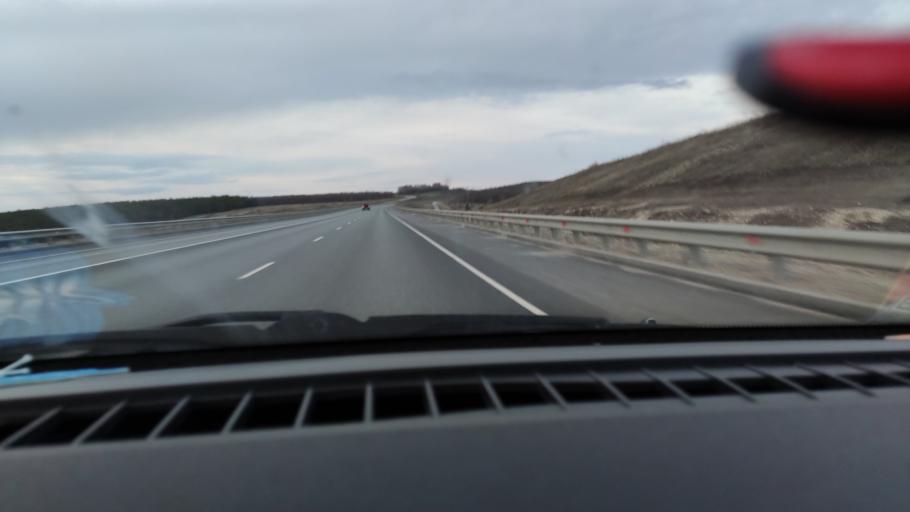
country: RU
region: Saratov
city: Yelshanka
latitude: 51.8806
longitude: 46.5097
